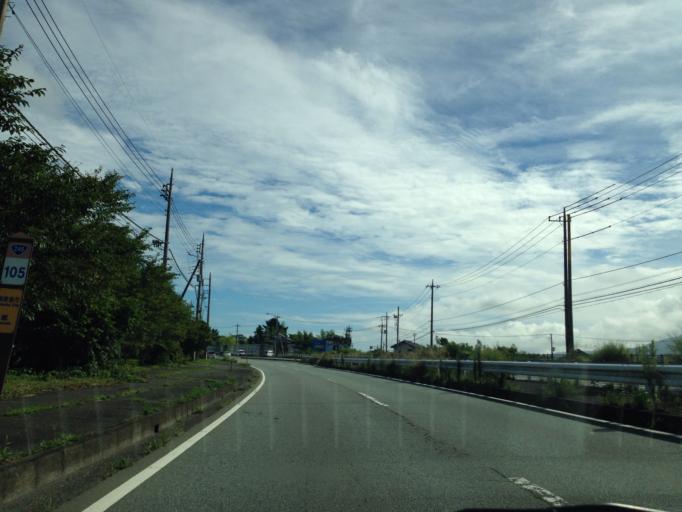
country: JP
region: Shizuoka
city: Gotemba
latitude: 35.2779
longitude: 138.9170
